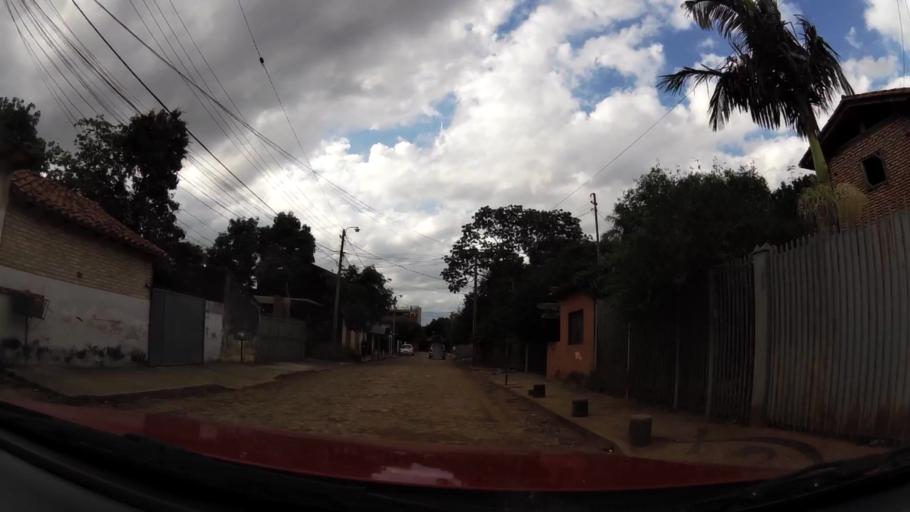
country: PY
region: Central
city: San Lorenzo
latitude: -25.2763
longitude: -57.4890
